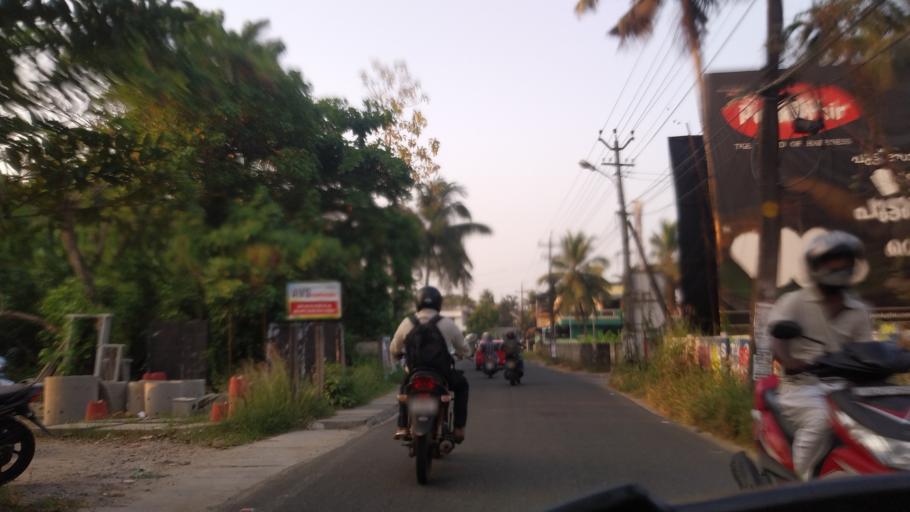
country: IN
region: Kerala
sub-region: Ernakulam
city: Elur
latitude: 10.0364
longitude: 76.2755
